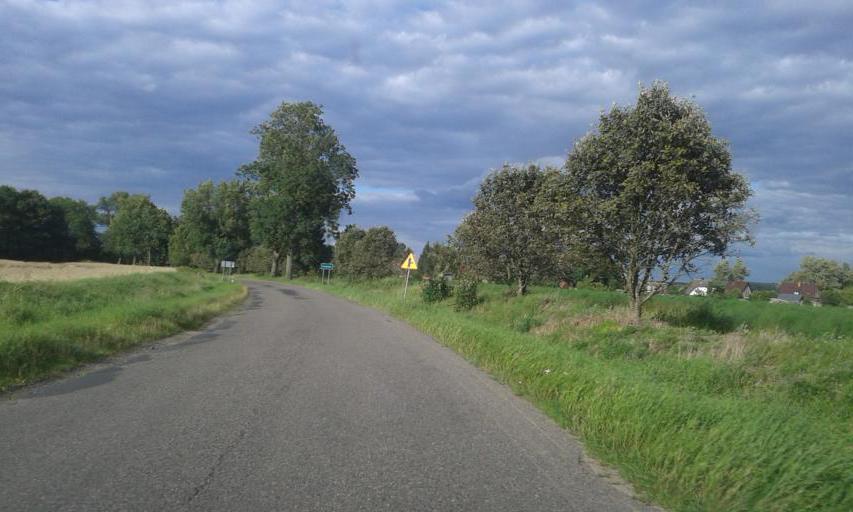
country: PL
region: West Pomeranian Voivodeship
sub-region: Powiat bialogardzki
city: Tychowo
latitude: 53.9061
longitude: 16.2408
